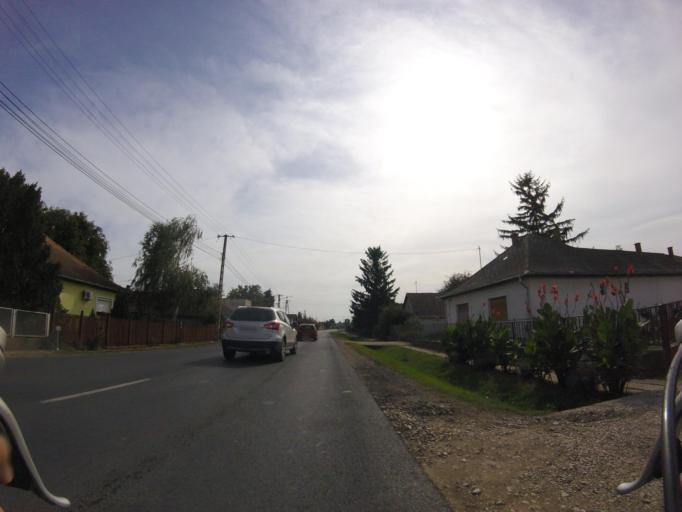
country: HU
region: Fejer
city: Sarbogard
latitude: 46.8636
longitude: 18.6289
